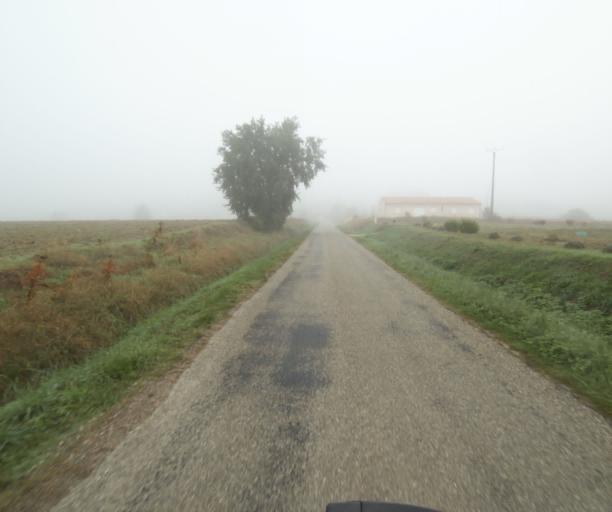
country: FR
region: Midi-Pyrenees
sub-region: Departement de la Haute-Garonne
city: Villemur-sur-Tarn
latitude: 43.9113
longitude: 1.4835
